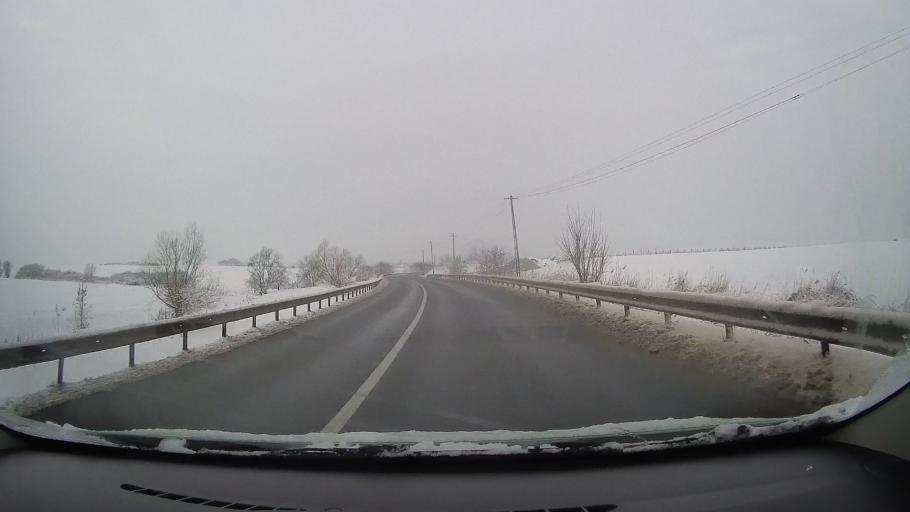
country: RO
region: Alba
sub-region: Municipiul Sebes
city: Lancram
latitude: 45.9831
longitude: 23.5160
